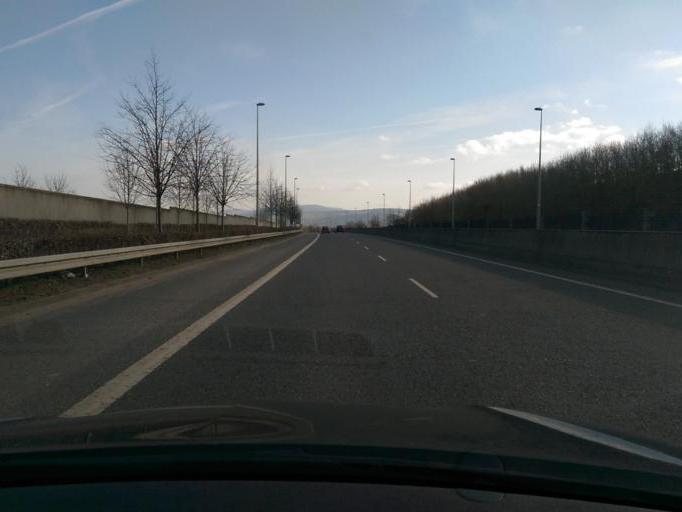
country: IE
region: Leinster
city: Clondalkin
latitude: 53.3232
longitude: -6.4313
